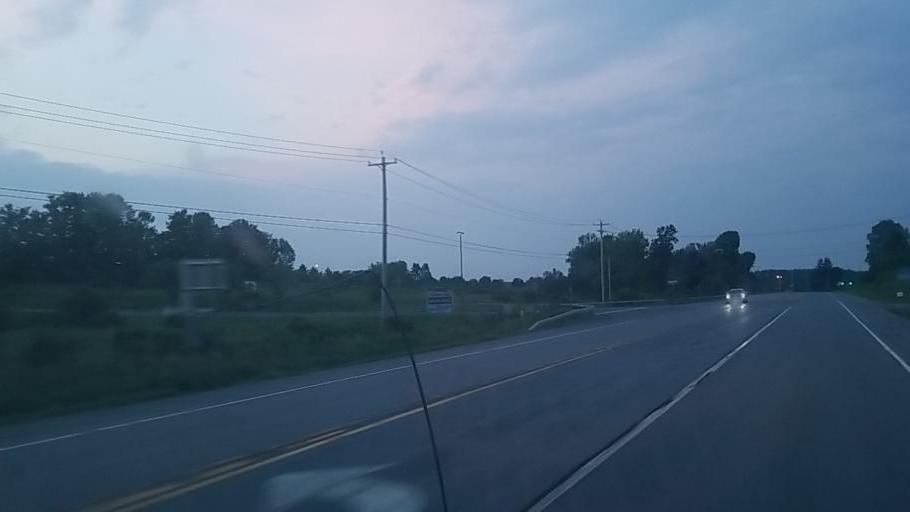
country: US
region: New York
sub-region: Fulton County
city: Johnstown
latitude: 42.9839
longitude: -74.3887
